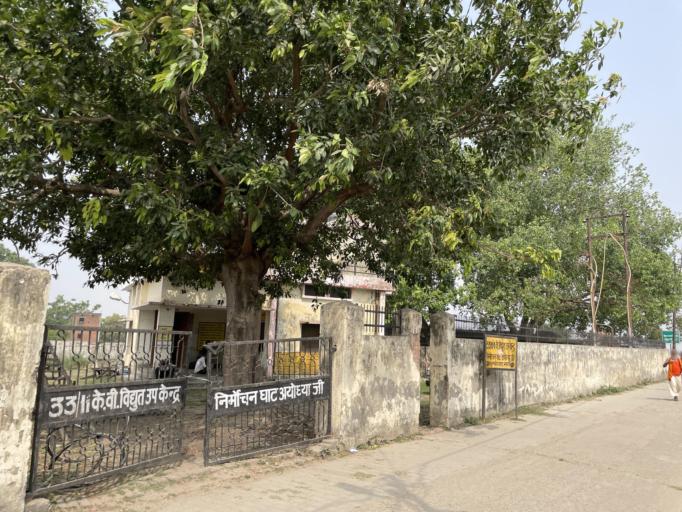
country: IN
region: Uttar Pradesh
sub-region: Faizabad
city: Ayodhya
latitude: 26.8057
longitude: 82.1982
